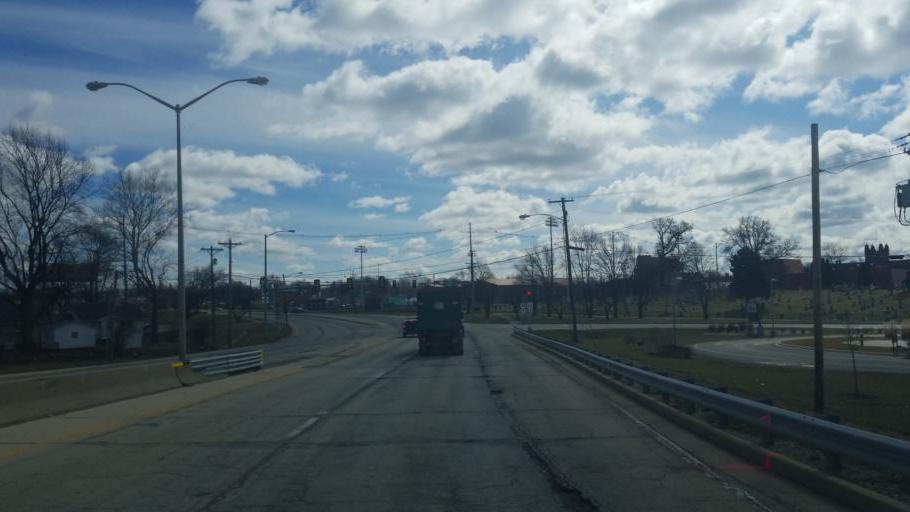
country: US
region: Illinois
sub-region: Macon County
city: Decatur
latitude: 39.8464
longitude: -88.9764
